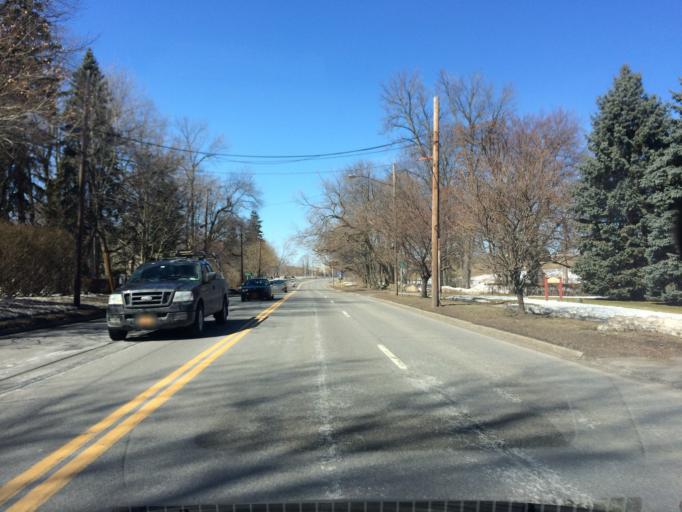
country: US
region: New York
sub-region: Monroe County
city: Brighton
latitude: 43.1409
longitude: -77.5448
